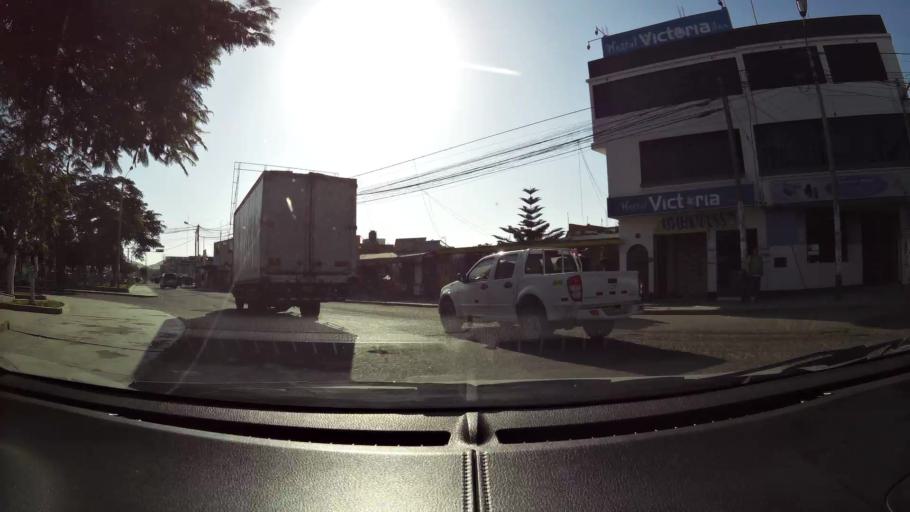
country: PE
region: Ancash
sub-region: Provincia de Casma
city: Casma
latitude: -9.4744
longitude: -78.2961
